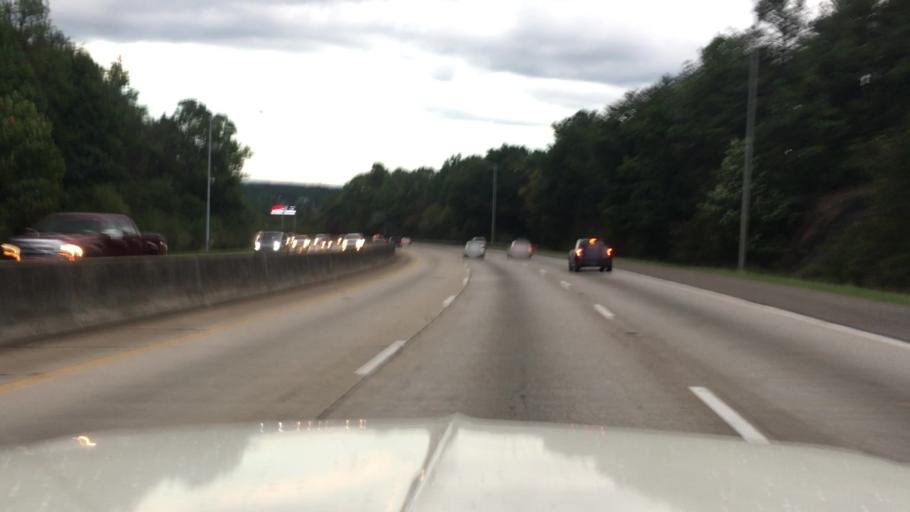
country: US
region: Alabama
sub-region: Jefferson County
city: Hoover
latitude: 33.4164
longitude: -86.8121
